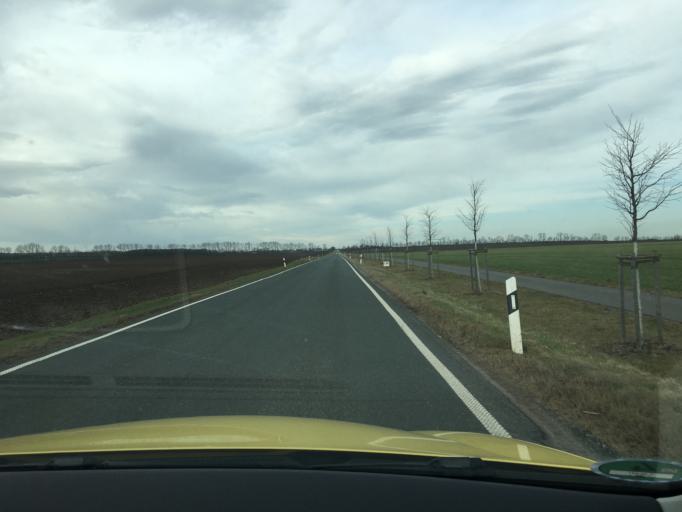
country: DE
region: Thuringia
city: Schwerstedt
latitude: 51.0713
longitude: 11.2857
